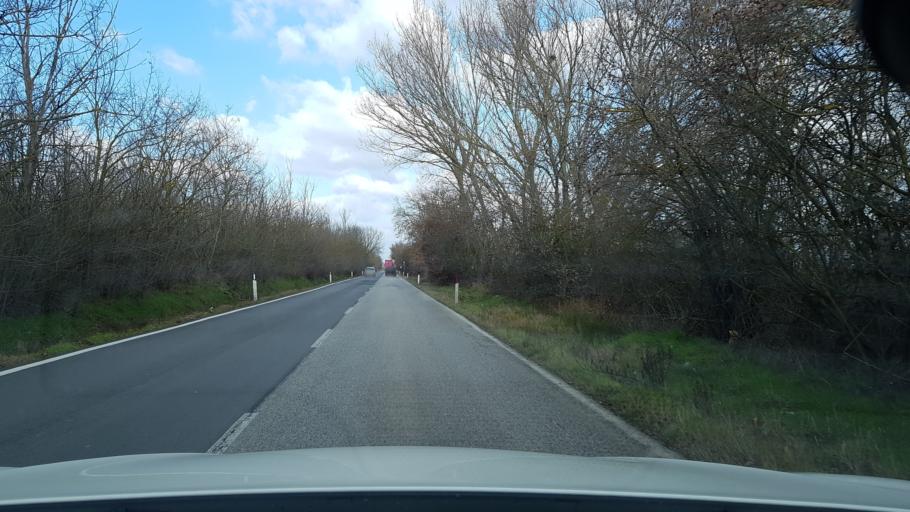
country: IT
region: Umbria
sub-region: Provincia di Perugia
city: Castiglione del Lago
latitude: 43.1360
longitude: 12.0269
